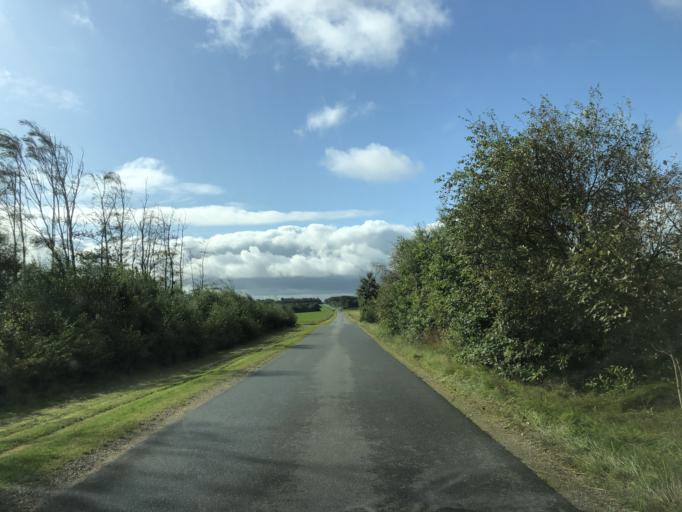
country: DK
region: Central Jutland
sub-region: Holstebro Kommune
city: Ulfborg
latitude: 56.3143
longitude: 8.4650
